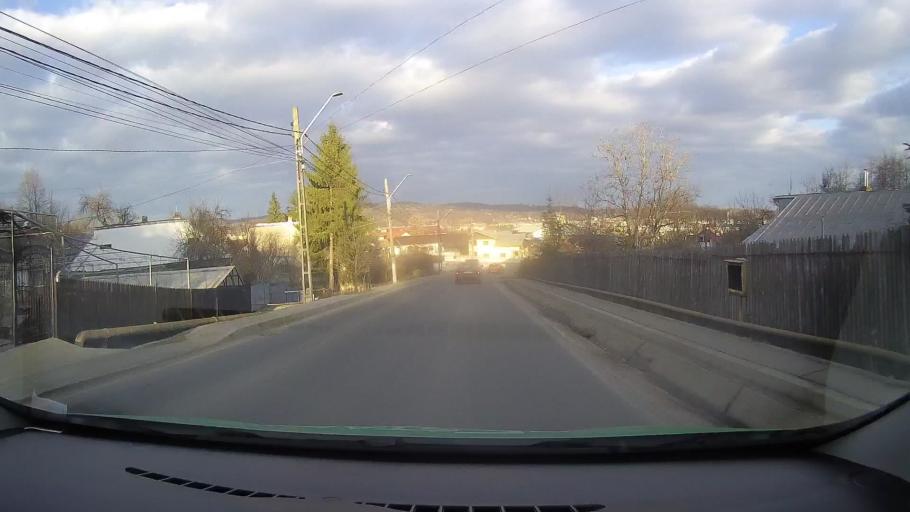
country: RO
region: Dambovita
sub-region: Municipiul Moreni
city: Moreni
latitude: 44.9813
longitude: 25.6312
